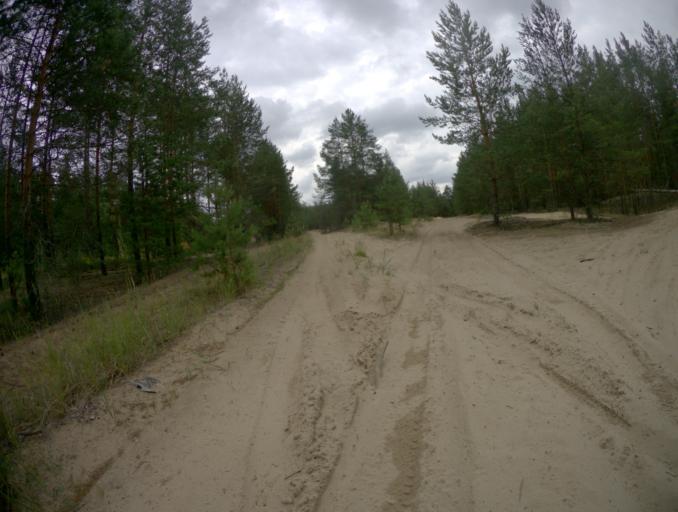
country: RU
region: Nizjnij Novgorod
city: Frolishchi
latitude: 56.3924
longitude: 42.6401
